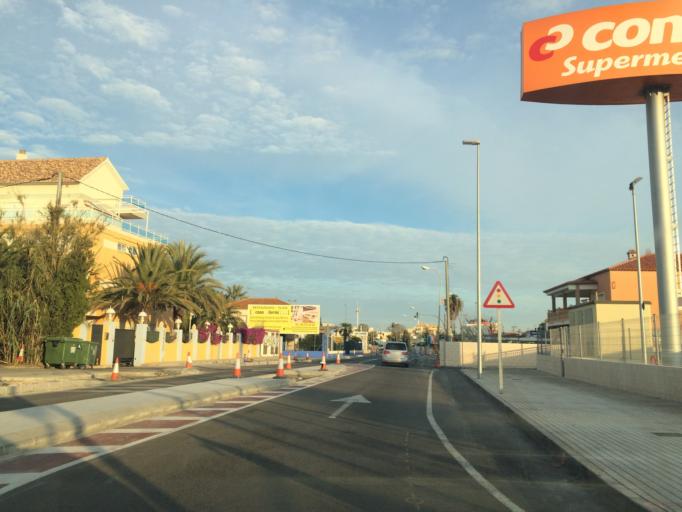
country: ES
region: Valencia
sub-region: Provincia de Alicante
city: els Poblets
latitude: 38.8586
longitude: 0.0572
